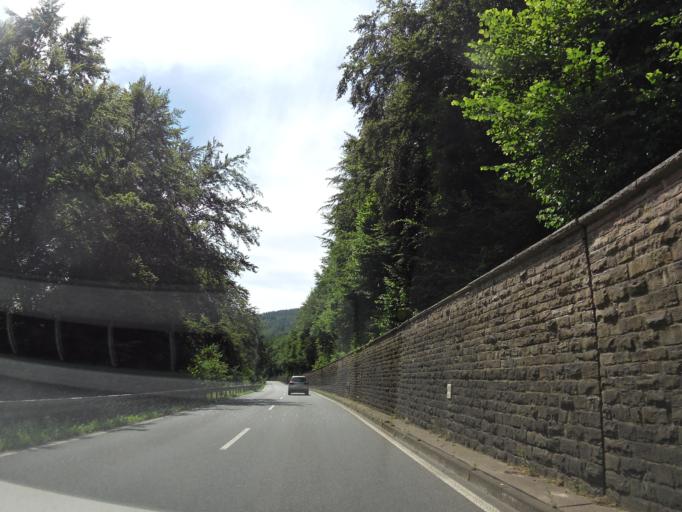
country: DE
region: Lower Saxony
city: Bodenfelde
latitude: 51.6075
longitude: 9.5369
